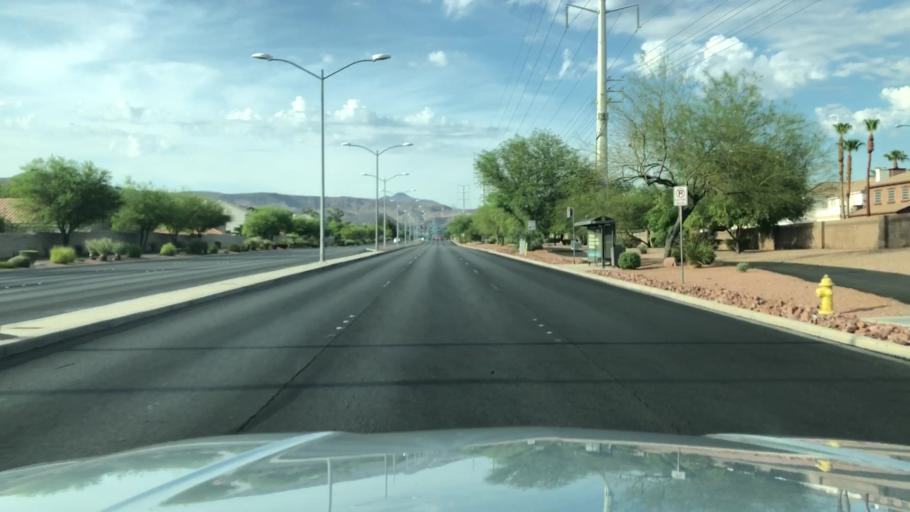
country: US
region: Nevada
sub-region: Clark County
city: Whitney
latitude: 36.0488
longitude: -115.0466
